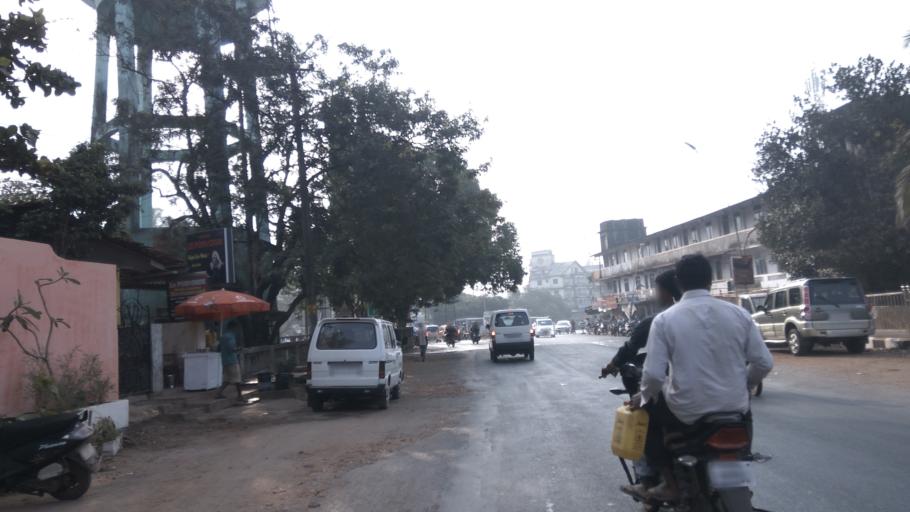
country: IN
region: Goa
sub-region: North Goa
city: Serula
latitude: 15.5318
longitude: 73.8242
